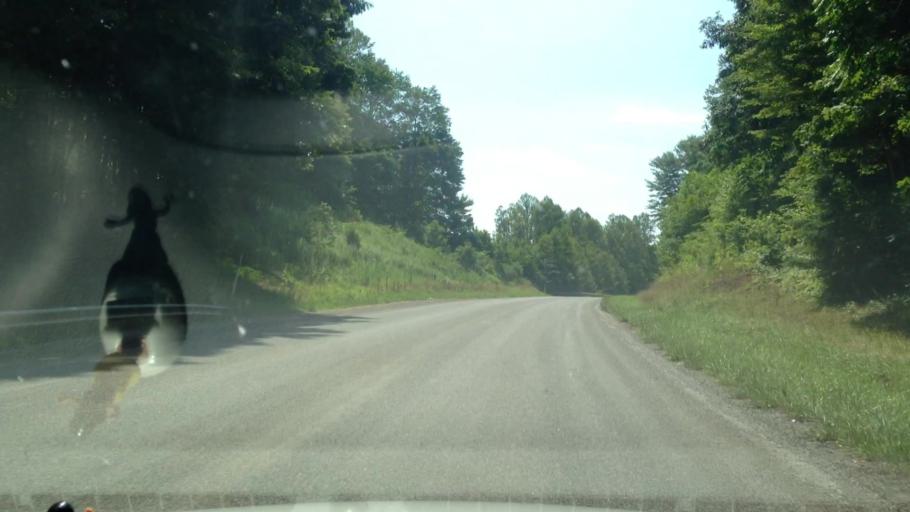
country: US
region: Virginia
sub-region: Patrick County
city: Stuart
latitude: 36.5985
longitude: -80.2984
